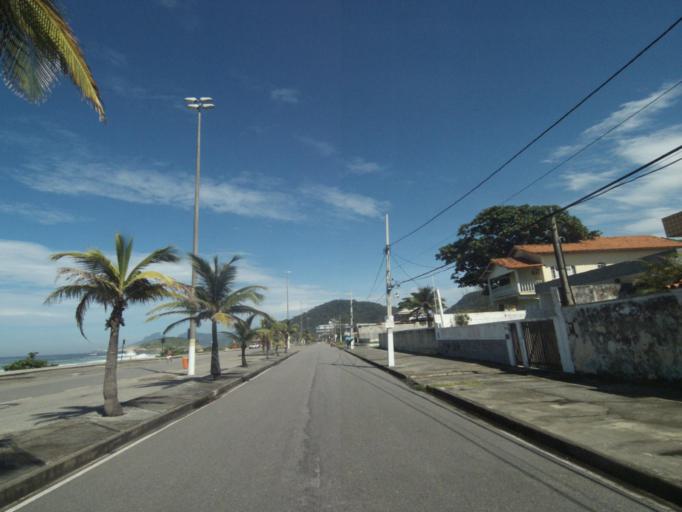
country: BR
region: Rio de Janeiro
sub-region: Niteroi
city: Niteroi
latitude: -22.9536
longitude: -43.0912
